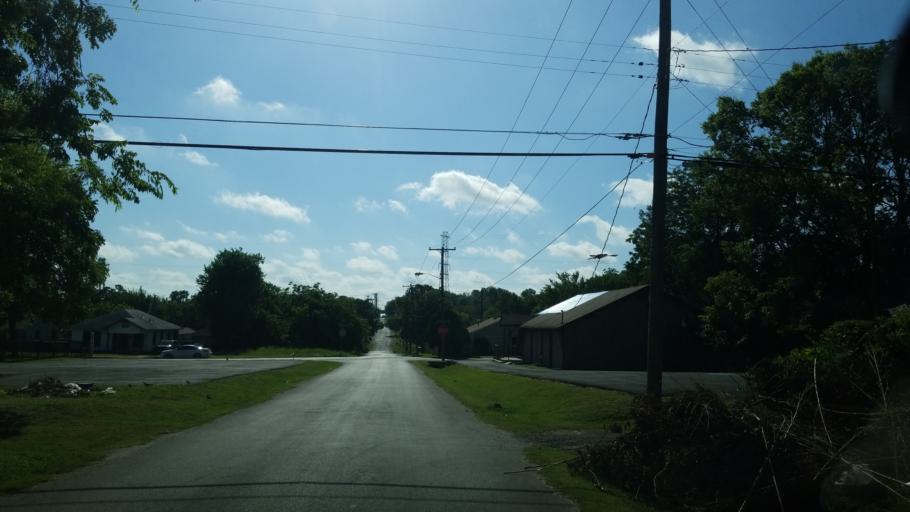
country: US
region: Texas
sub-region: Dallas County
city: Dallas
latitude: 32.7191
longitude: -96.8105
